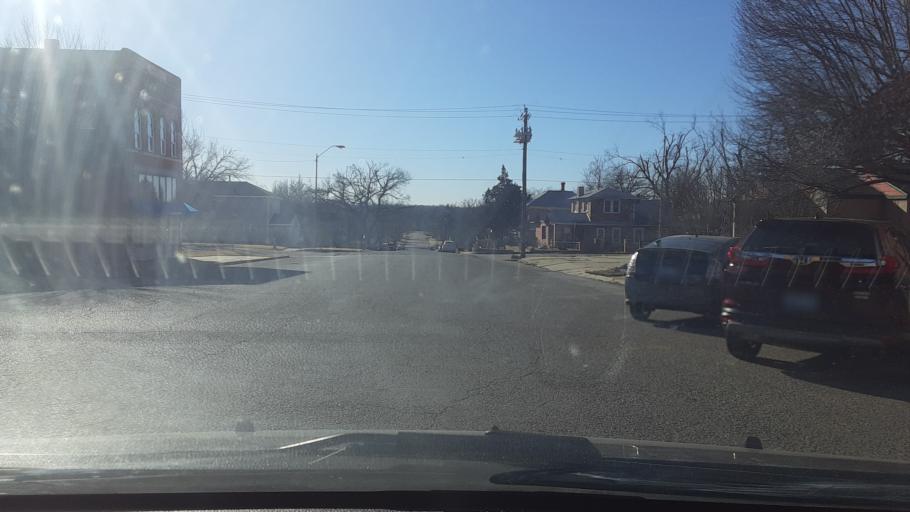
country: US
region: Oklahoma
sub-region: Logan County
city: Guthrie
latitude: 35.8765
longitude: -97.4276
